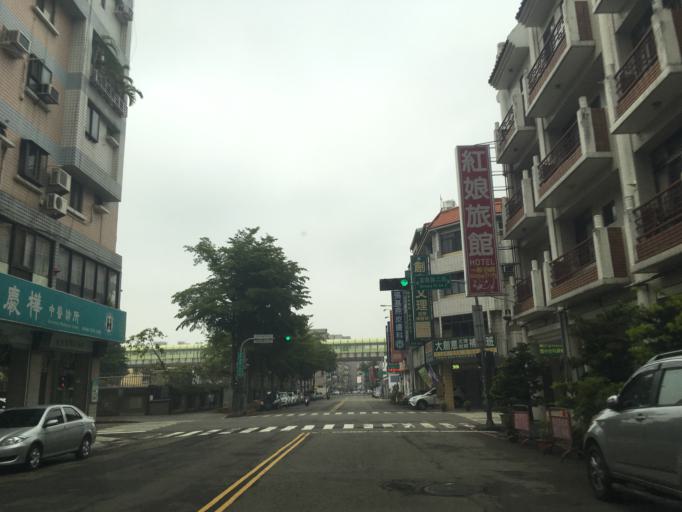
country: TW
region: Taiwan
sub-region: Taichung City
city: Taichung
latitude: 24.1741
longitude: 120.6818
